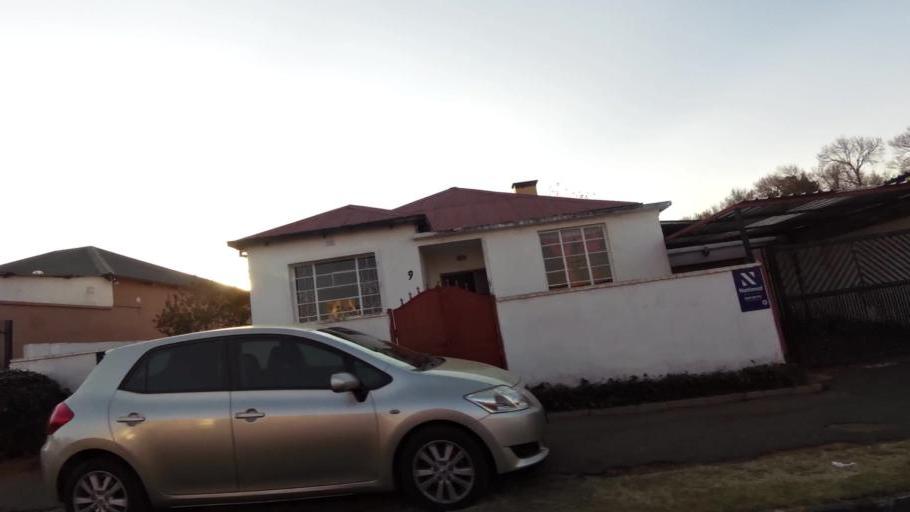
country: ZA
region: Gauteng
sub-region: City of Johannesburg Metropolitan Municipality
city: Johannesburg
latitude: -26.1732
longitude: 27.9635
